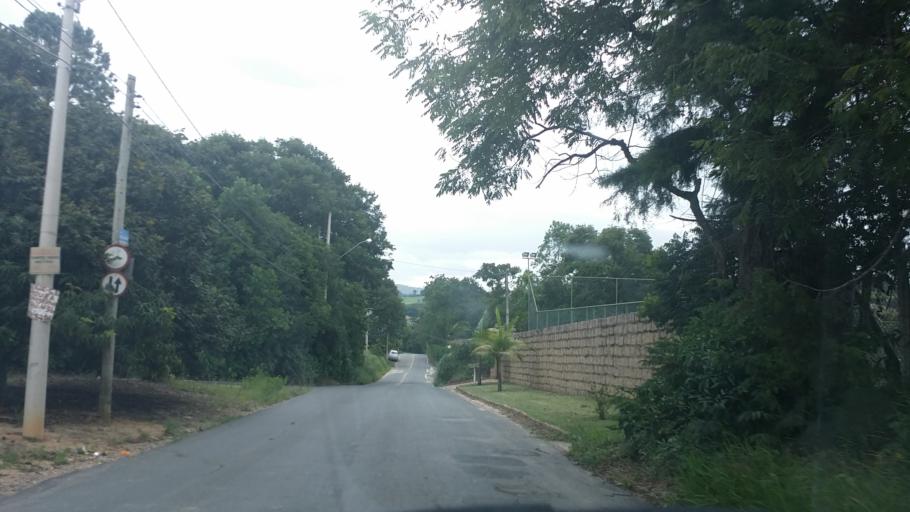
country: BR
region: Sao Paulo
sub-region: Itupeva
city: Itupeva
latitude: -23.1742
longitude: -47.1104
